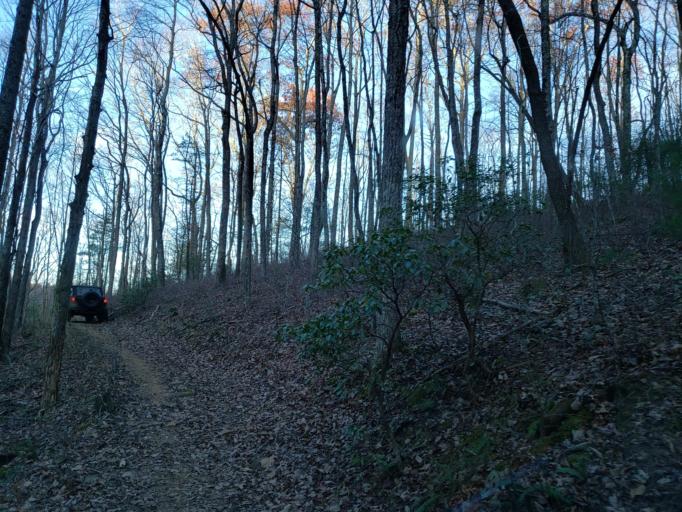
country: US
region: Georgia
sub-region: Lumpkin County
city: Dahlonega
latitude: 34.6670
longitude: -84.1028
